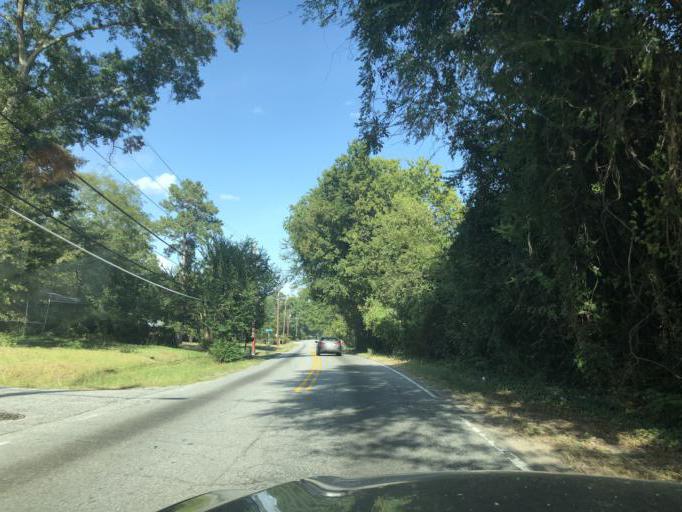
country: US
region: Georgia
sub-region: Muscogee County
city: Columbus
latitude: 32.4848
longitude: -84.9142
